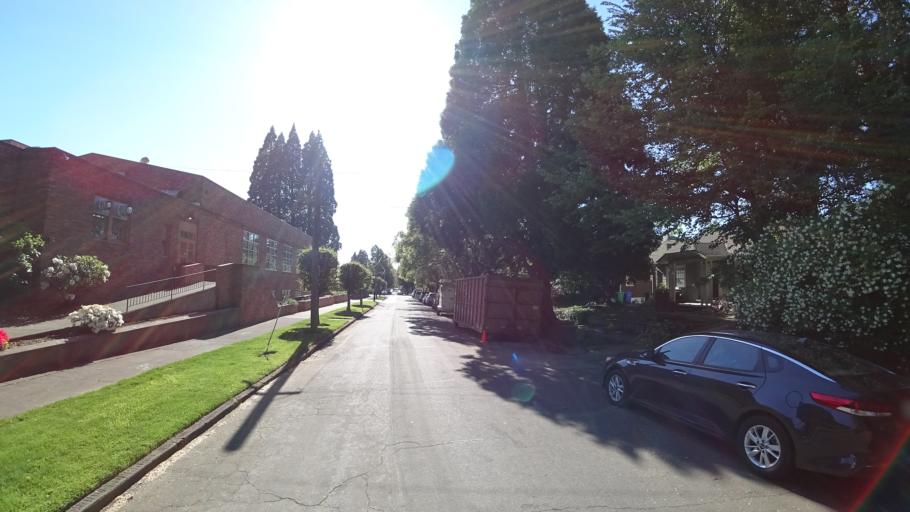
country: US
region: Oregon
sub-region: Multnomah County
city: Portland
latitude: 45.5271
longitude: -122.6317
